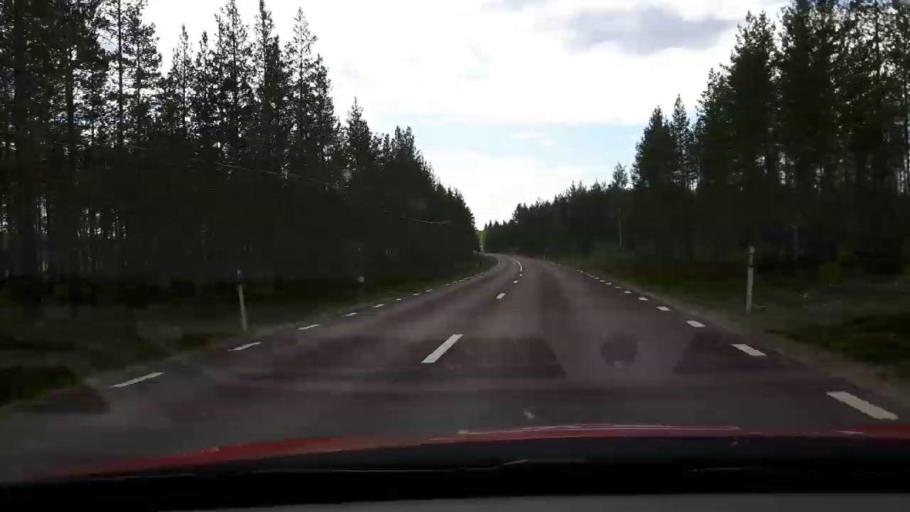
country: SE
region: Jaemtland
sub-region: Harjedalens Kommun
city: Sveg
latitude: 62.1202
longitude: 14.9701
